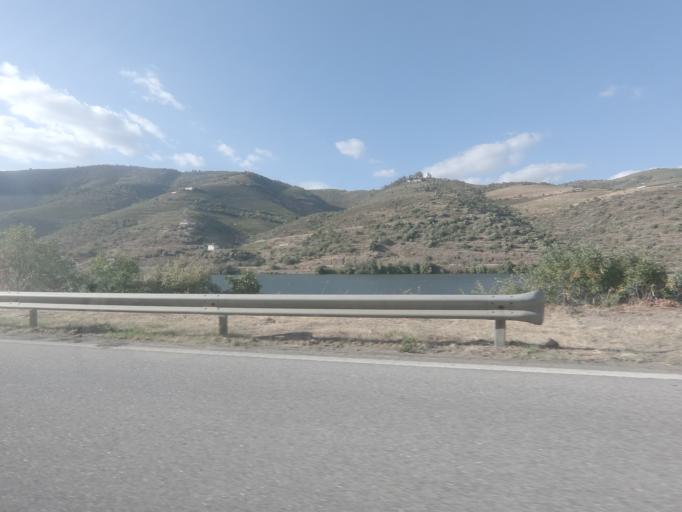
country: PT
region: Viseu
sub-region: Tabuaco
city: Tabuaco
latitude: 41.1579
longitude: -7.6077
